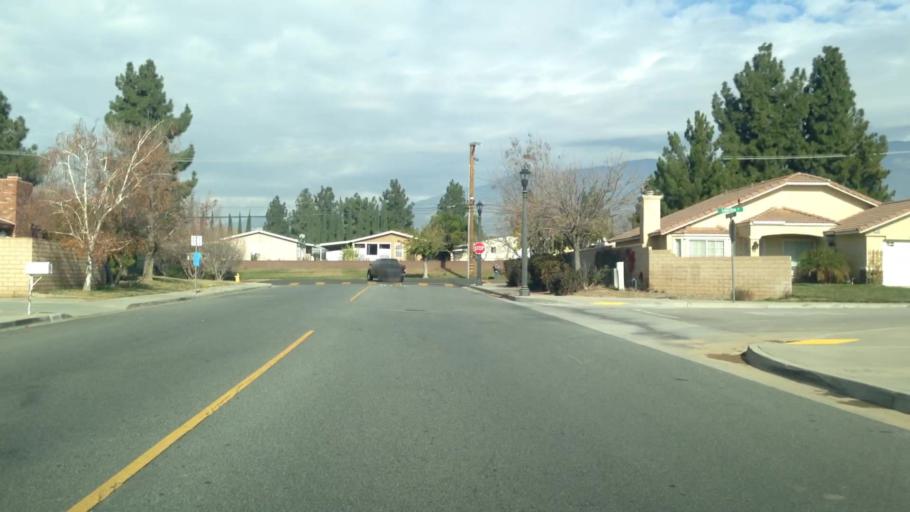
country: US
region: California
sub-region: Riverside County
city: Beaumont
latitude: 33.9462
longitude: -116.9661
